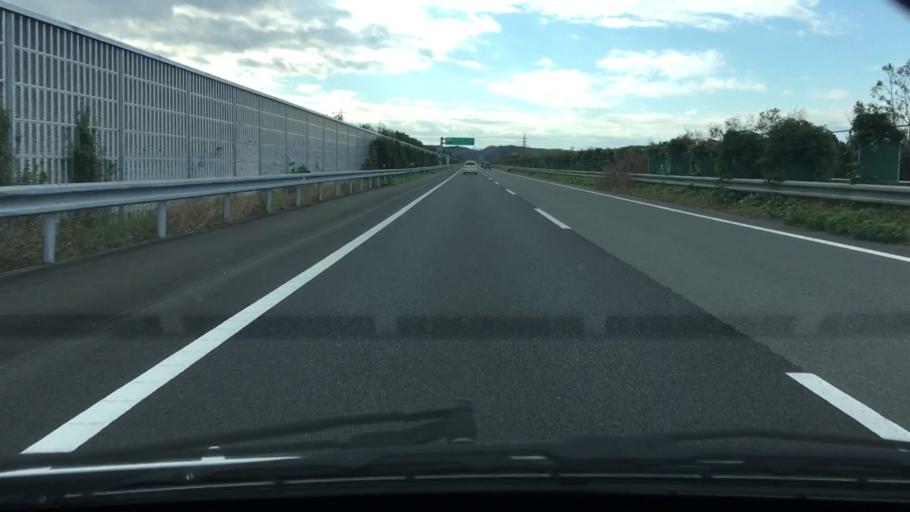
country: JP
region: Chiba
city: Kisarazu
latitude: 35.4044
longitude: 140.0078
